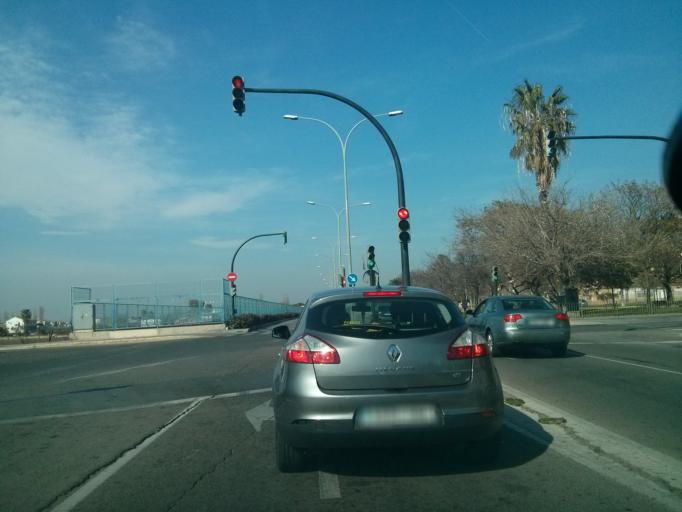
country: ES
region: Valencia
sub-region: Provincia de Valencia
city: Alboraya
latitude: 39.4804
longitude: -0.3326
